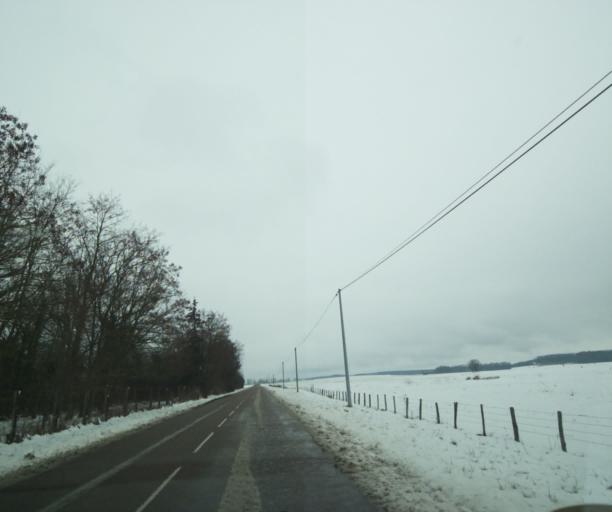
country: FR
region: Champagne-Ardenne
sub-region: Departement de la Haute-Marne
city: Montier-en-Der
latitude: 48.4516
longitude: 4.7771
